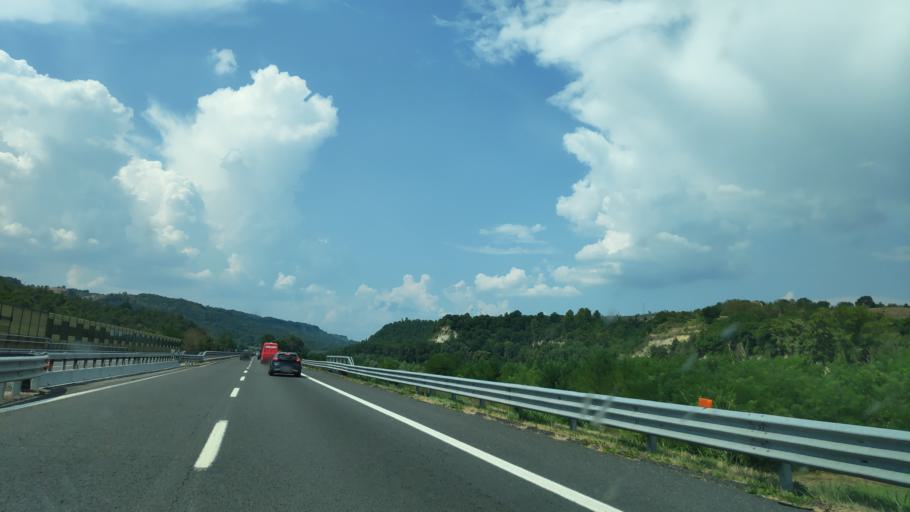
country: IT
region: Umbria
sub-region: Provincia di Terni
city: Baschi
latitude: 42.6998
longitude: 12.1801
